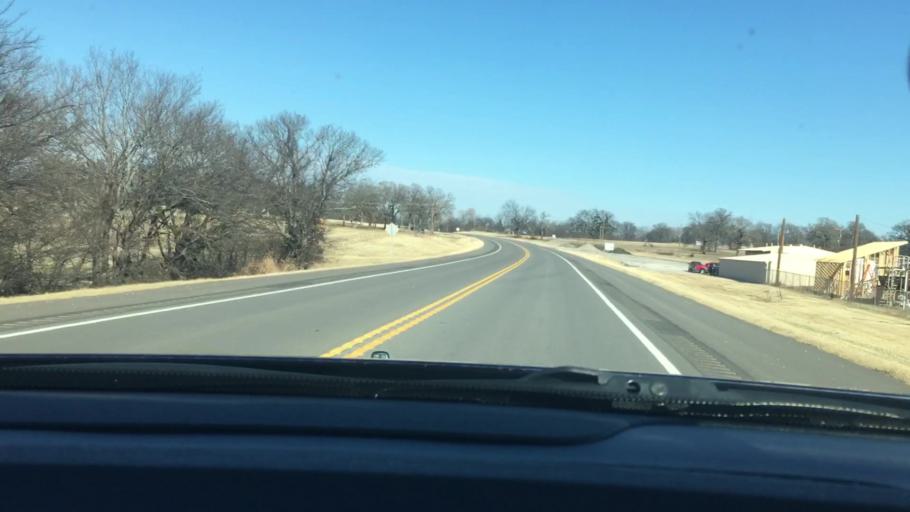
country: US
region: Oklahoma
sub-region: Murray County
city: Davis
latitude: 34.5147
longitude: -97.1217
